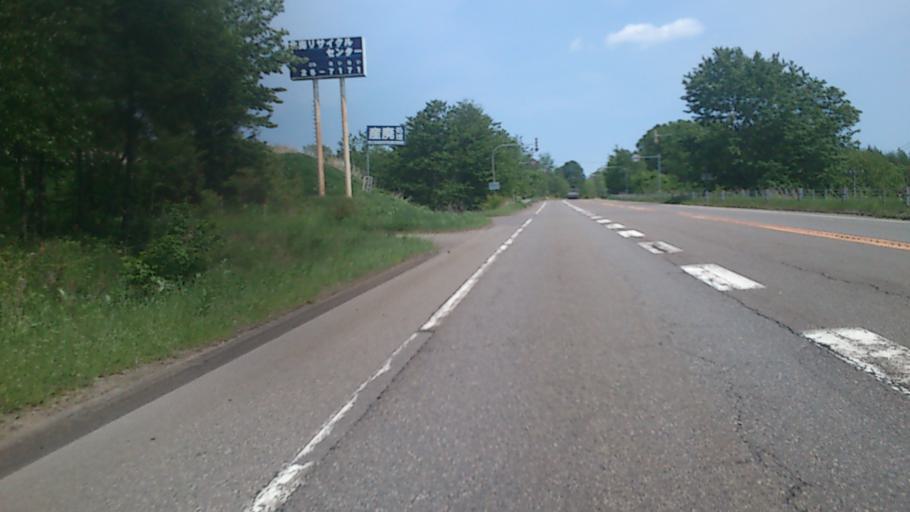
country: JP
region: Hokkaido
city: Otofuke
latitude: 43.2360
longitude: 143.4889
